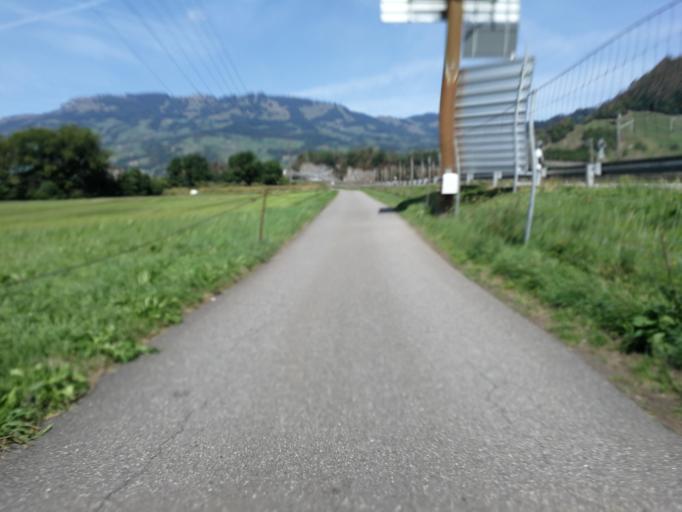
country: CH
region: Schwyz
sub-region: Bezirk Schwyz
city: Steinen
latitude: 47.0321
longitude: 8.6230
